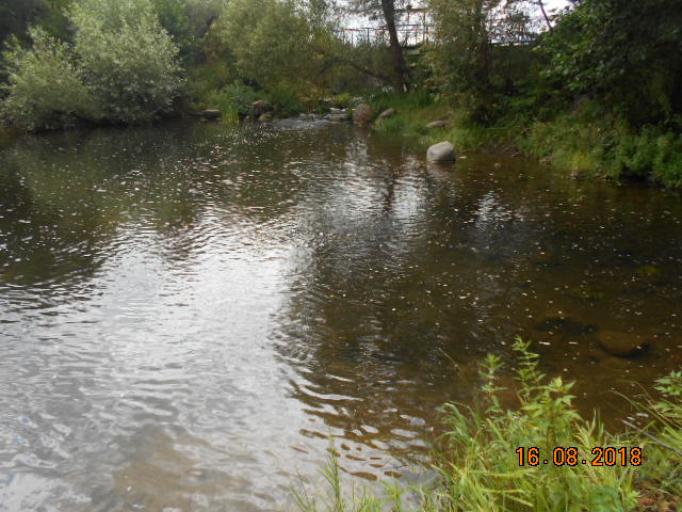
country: BY
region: Brest
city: Haradzishcha
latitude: 53.3351
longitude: 26.0145
